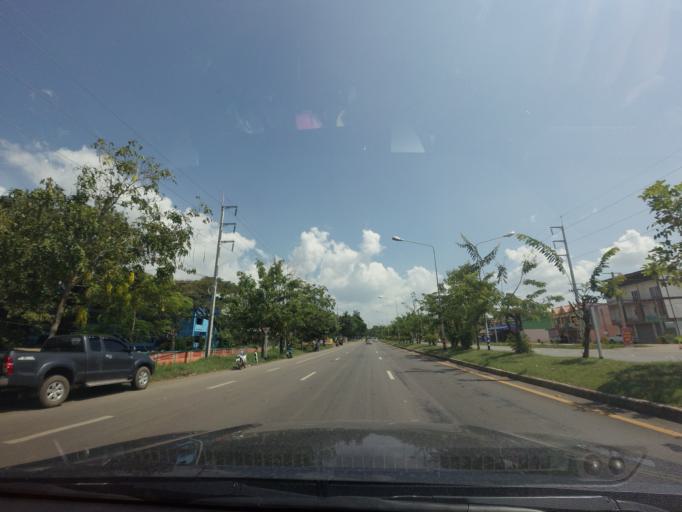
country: TH
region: Phetchabun
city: Nong Phai
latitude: 16.0775
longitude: 101.0632
